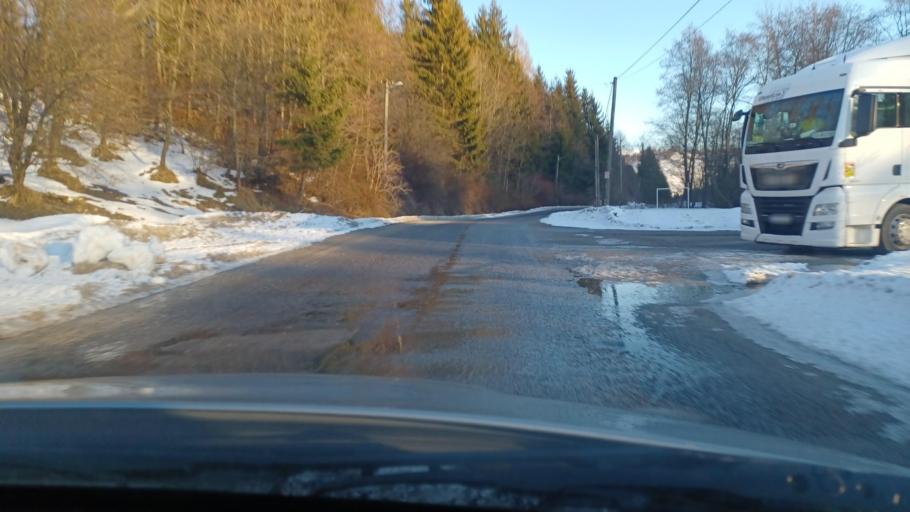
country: SK
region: Zilinsky
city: Tvrdosin
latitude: 49.3641
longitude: 19.5344
